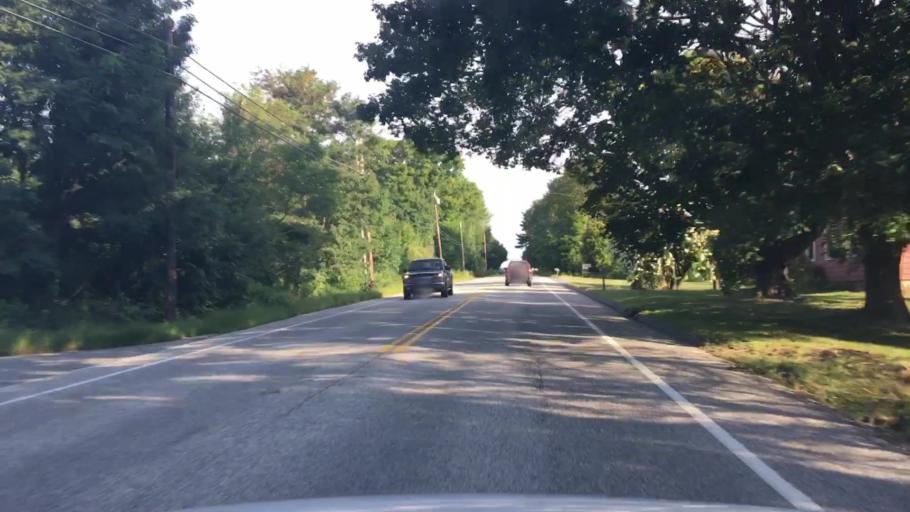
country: US
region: Maine
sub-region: Cumberland County
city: South Windham
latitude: 43.7411
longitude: -70.4211
